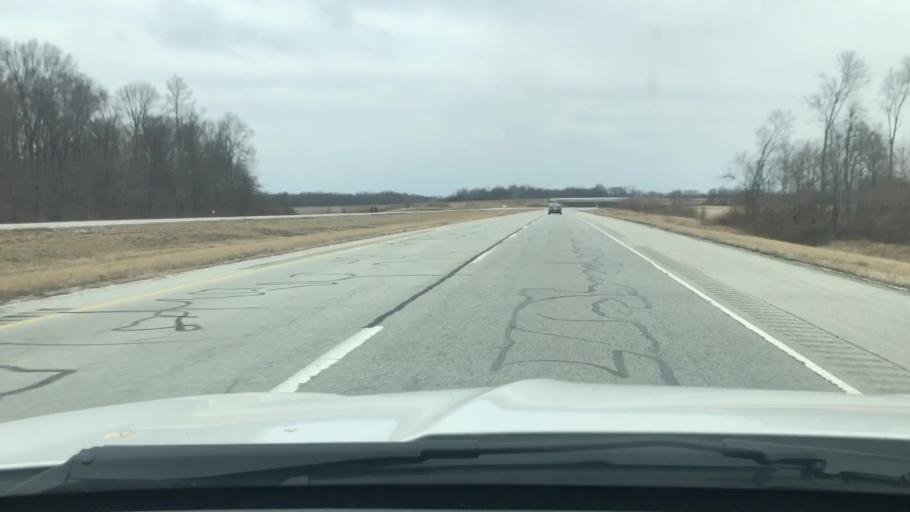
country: US
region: Indiana
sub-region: Carroll County
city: Delphi
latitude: 40.6394
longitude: -86.5820
